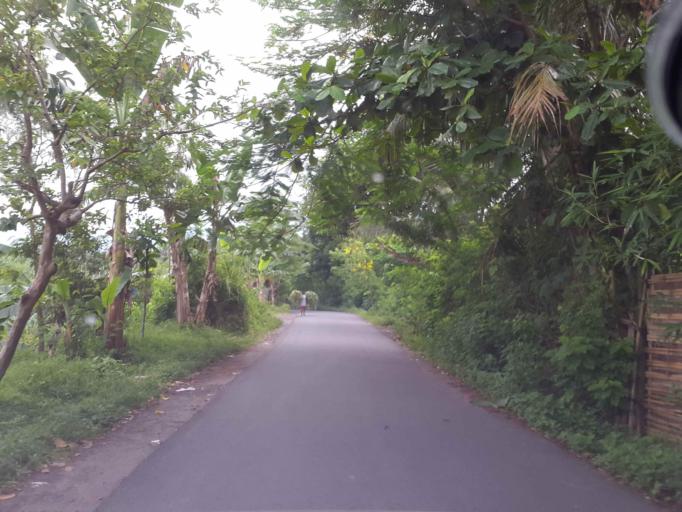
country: ID
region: West Nusa Tenggara
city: Dasangeria Selatan
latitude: -8.5536
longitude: 116.1474
